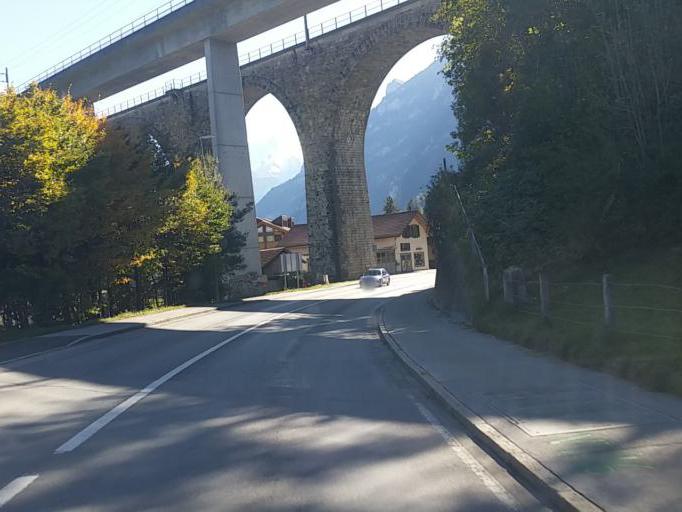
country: CH
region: Bern
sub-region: Frutigen-Niedersimmental District
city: Frutigen
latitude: 46.5764
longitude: 7.6535
